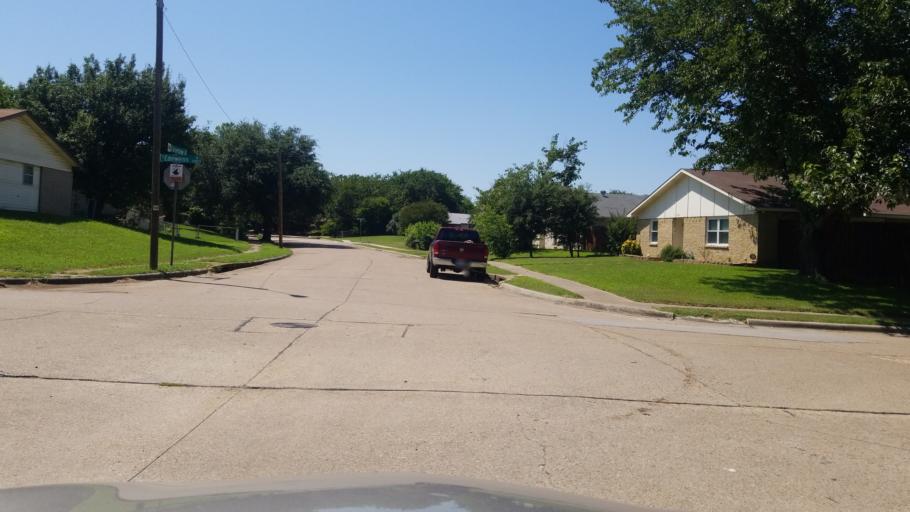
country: US
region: Texas
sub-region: Dallas County
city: Grand Prairie
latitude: 32.6914
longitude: -96.9952
